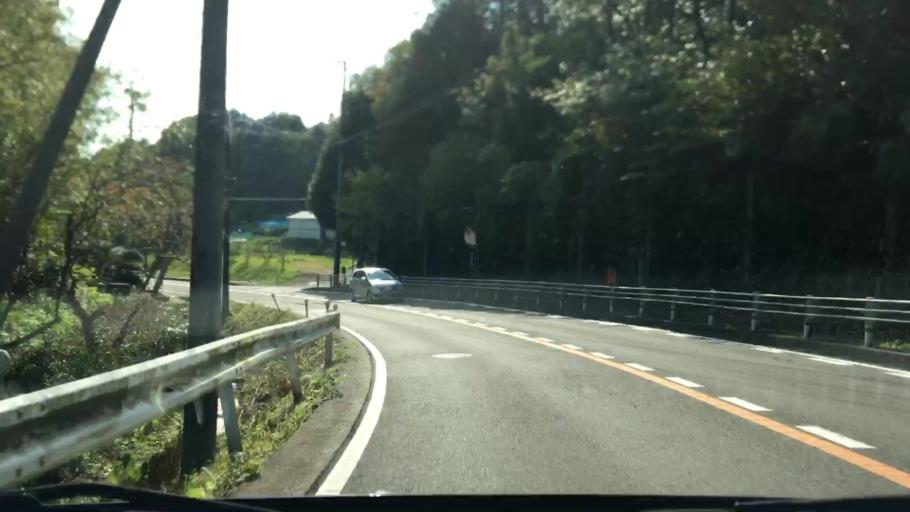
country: JP
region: Nagasaki
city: Togitsu
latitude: 32.9592
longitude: 129.7824
